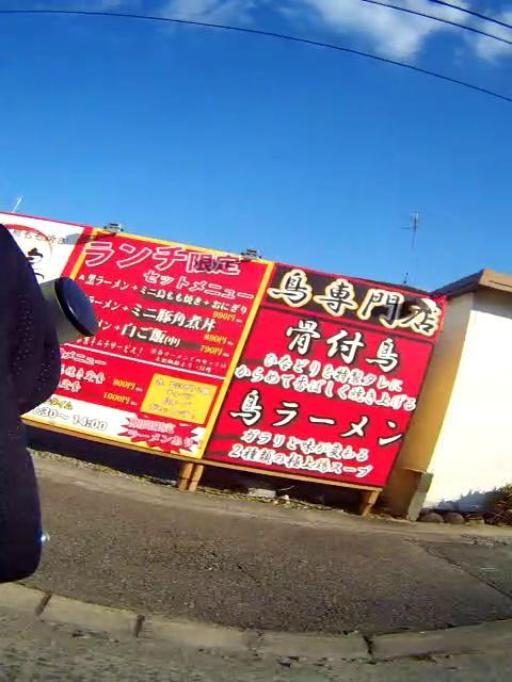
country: JP
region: Hyogo
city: Takarazuka
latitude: 34.7841
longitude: 135.3581
